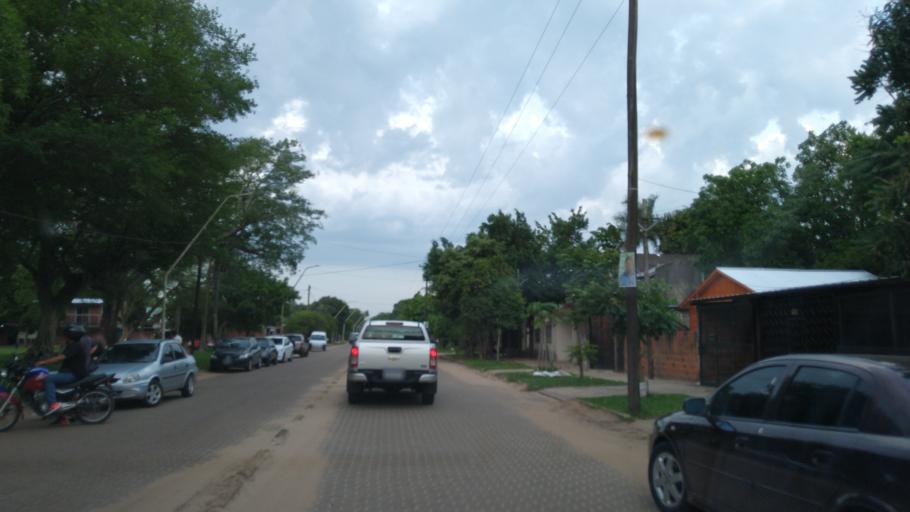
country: AR
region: Corrientes
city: Ituzaingo
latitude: -27.5896
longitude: -56.6987
